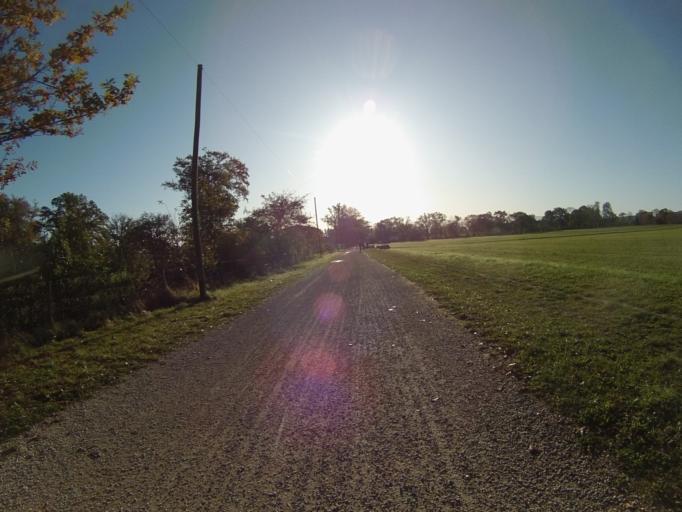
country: CH
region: Geneva
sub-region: Geneva
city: Meyrin
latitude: 46.2450
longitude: 6.0831
